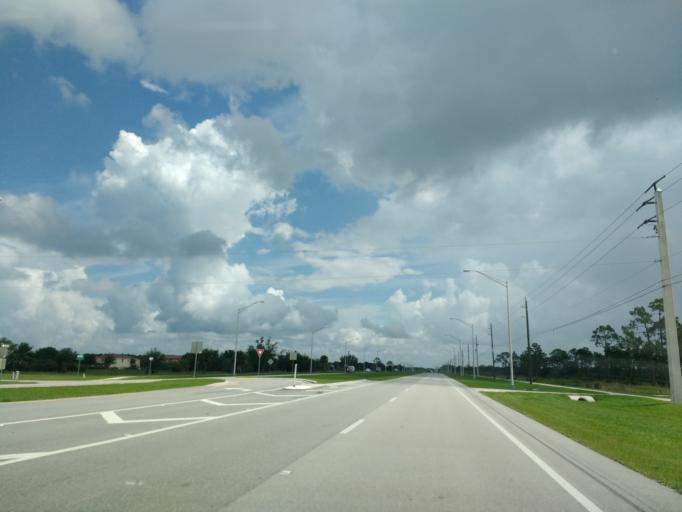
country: US
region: Florida
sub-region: Lee County
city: Burnt Store Marina
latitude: 26.7754
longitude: -82.0379
